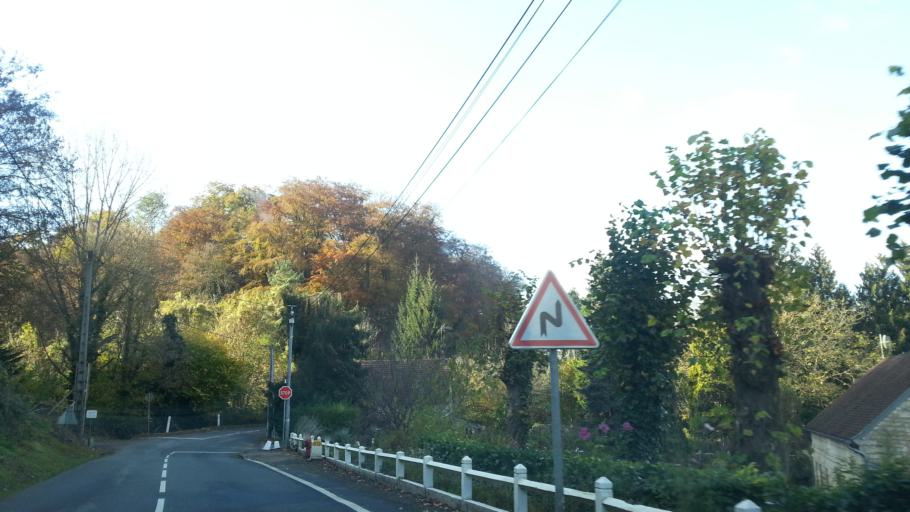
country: FR
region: Picardie
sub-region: Departement de l'Oise
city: Thiverny
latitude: 49.2582
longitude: 2.3976
